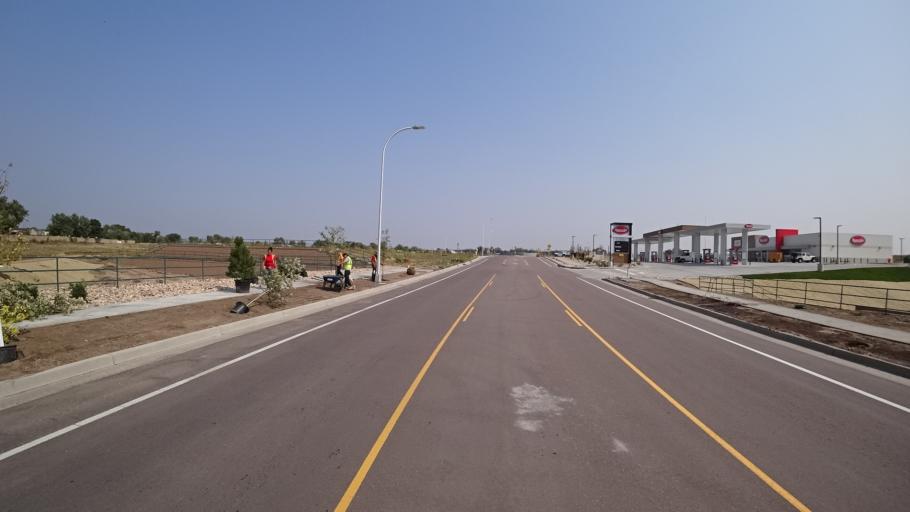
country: US
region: Colorado
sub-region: El Paso County
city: Cimarron Hills
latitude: 38.8261
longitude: -104.7287
